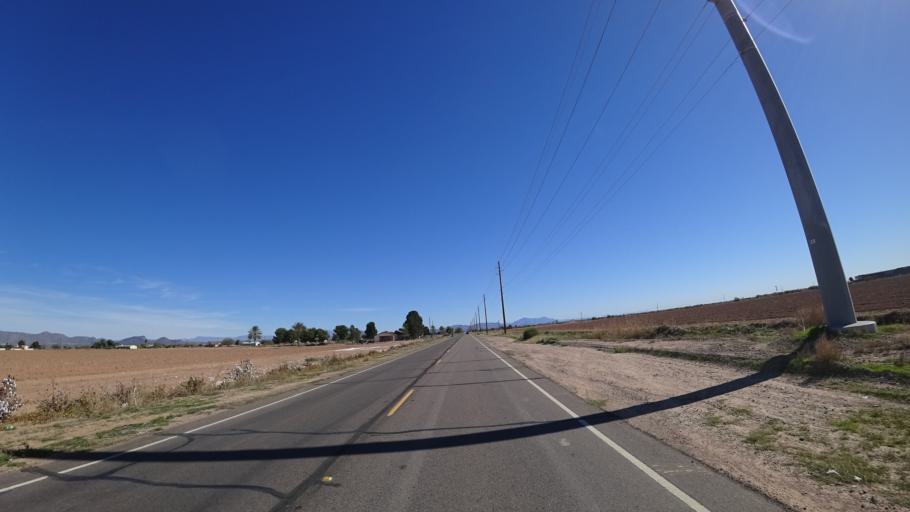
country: US
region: Arizona
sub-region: Maricopa County
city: Scottsdale
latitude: 33.4950
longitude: -111.8696
